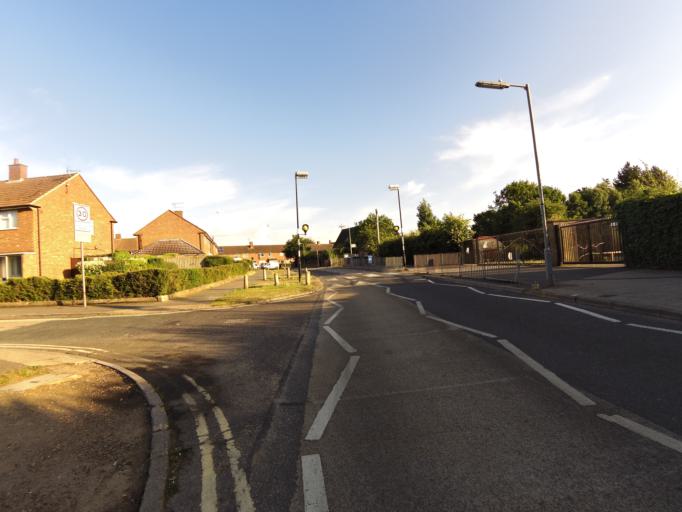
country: GB
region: England
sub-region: Suffolk
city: Ipswich
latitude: 52.0476
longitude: 1.1230
